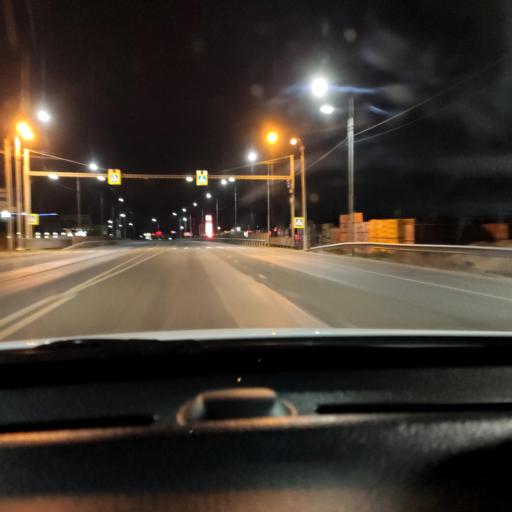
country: RU
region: Voronezj
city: Somovo
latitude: 51.6773
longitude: 39.3278
